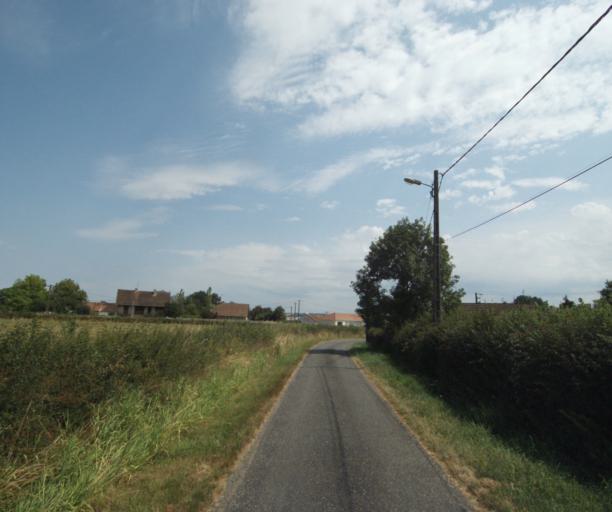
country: FR
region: Bourgogne
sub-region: Departement de Saone-et-Loire
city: Gueugnon
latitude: 46.6132
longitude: 4.0389
